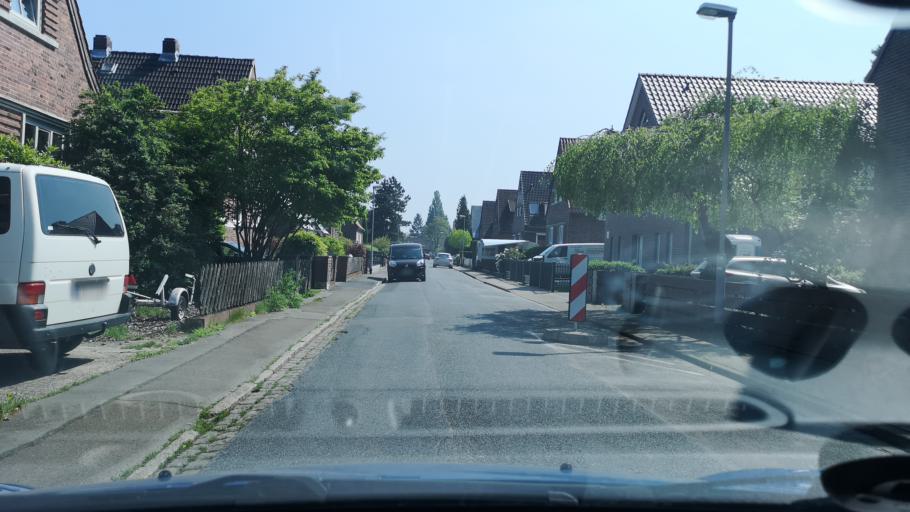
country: DE
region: Lower Saxony
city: Langenhagen
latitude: 52.4152
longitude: 9.7072
